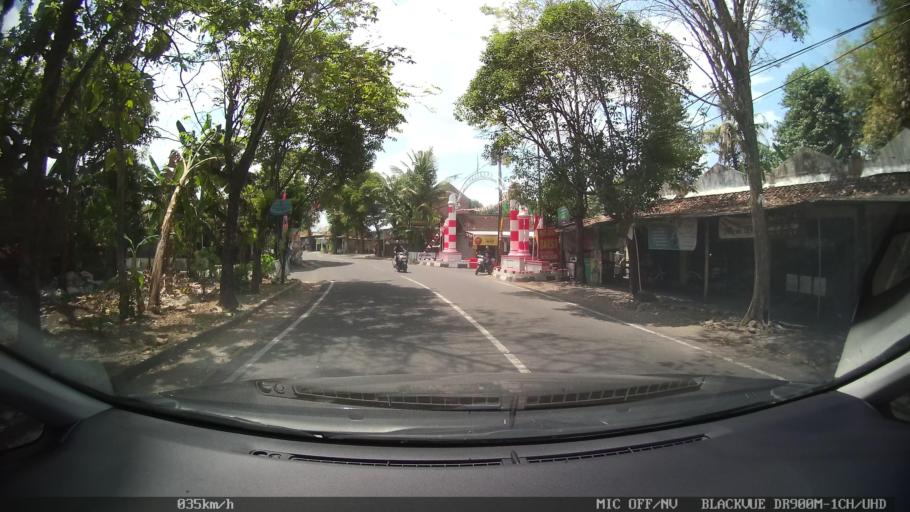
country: ID
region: Daerah Istimewa Yogyakarta
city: Bantul
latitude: -7.8858
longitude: 110.3352
